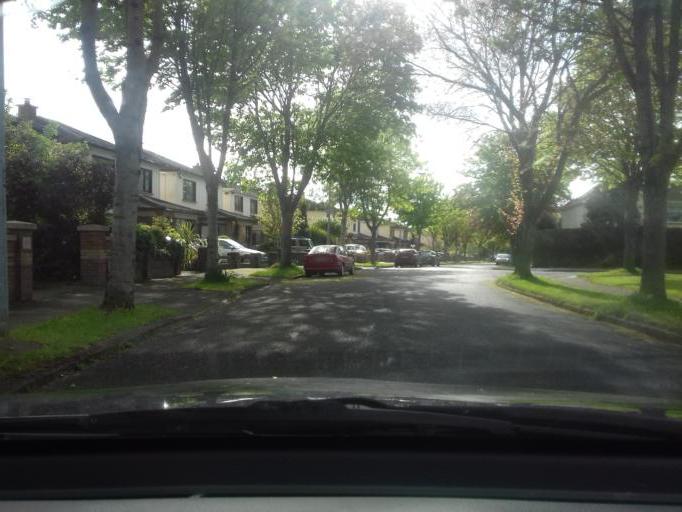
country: IE
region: Leinster
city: Castleknock
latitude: 53.3731
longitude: -6.3675
